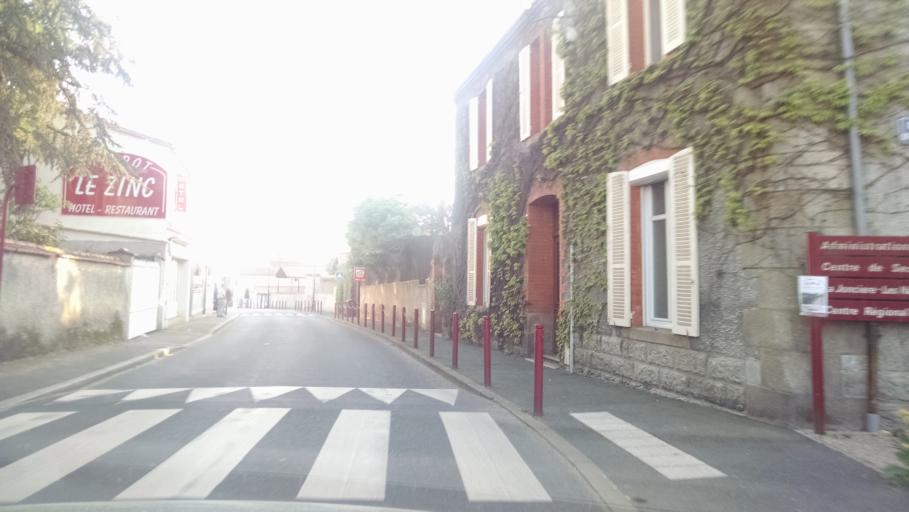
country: FR
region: Pays de la Loire
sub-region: Departement de la Loire-Atlantique
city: Boussay
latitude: 47.0434
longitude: -1.1869
